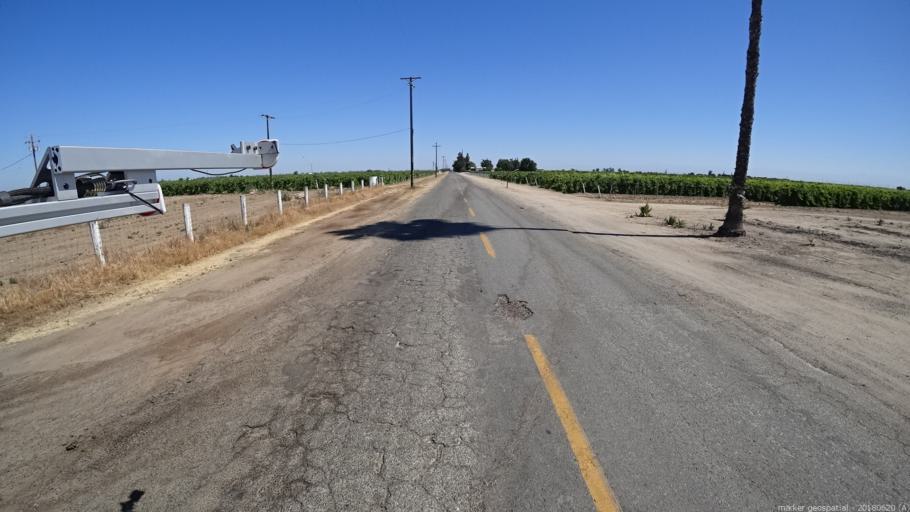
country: US
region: California
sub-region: Fresno County
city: Biola
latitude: 36.8559
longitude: -120.0193
